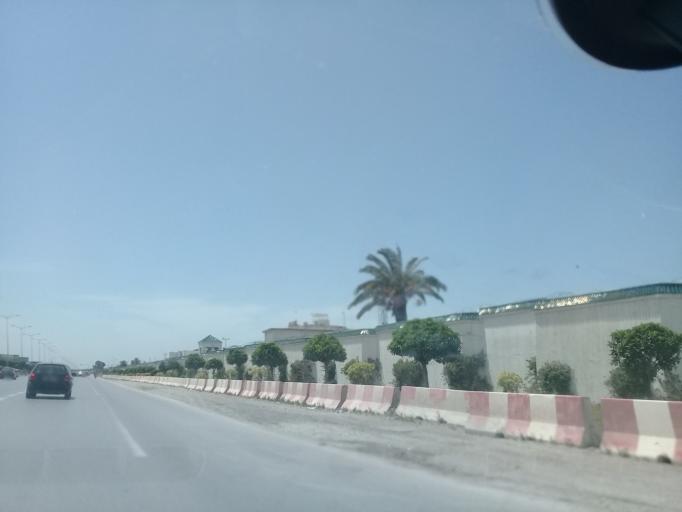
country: TN
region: Ariana
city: Ariana
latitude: 36.8408
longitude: 10.2416
